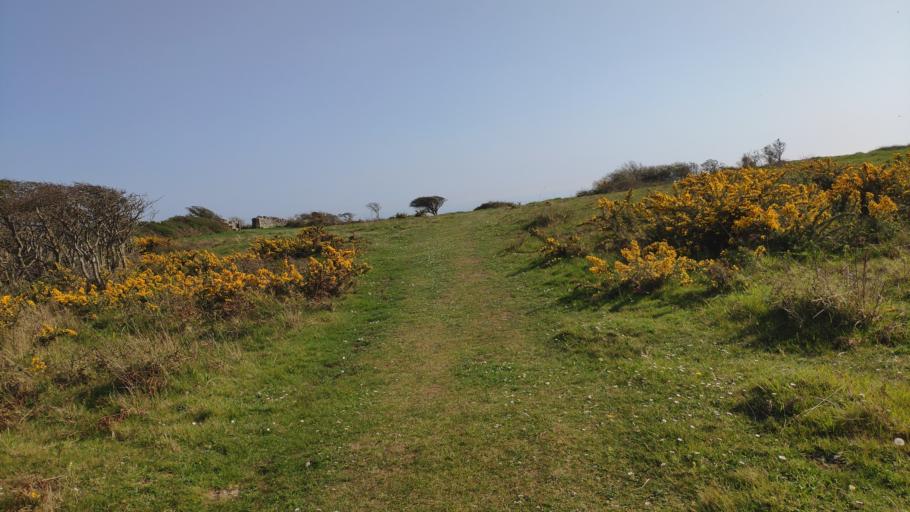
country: GB
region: England
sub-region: Dorset
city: Swanage
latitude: 50.5936
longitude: -1.9696
